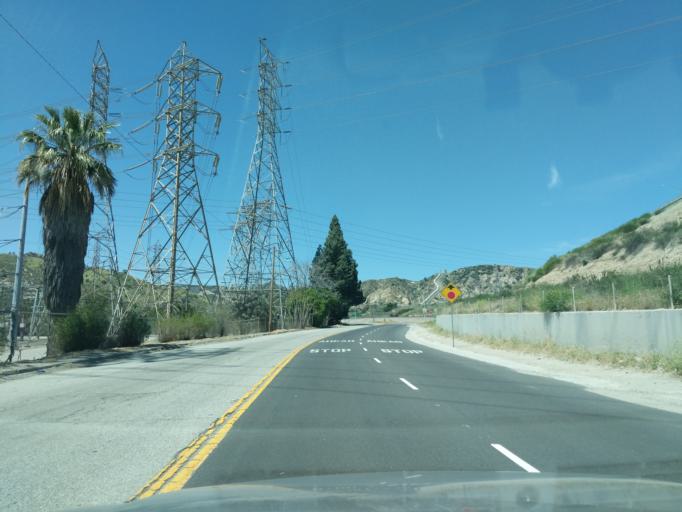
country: US
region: California
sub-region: Los Angeles County
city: San Fernando
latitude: 34.3137
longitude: -118.4903
